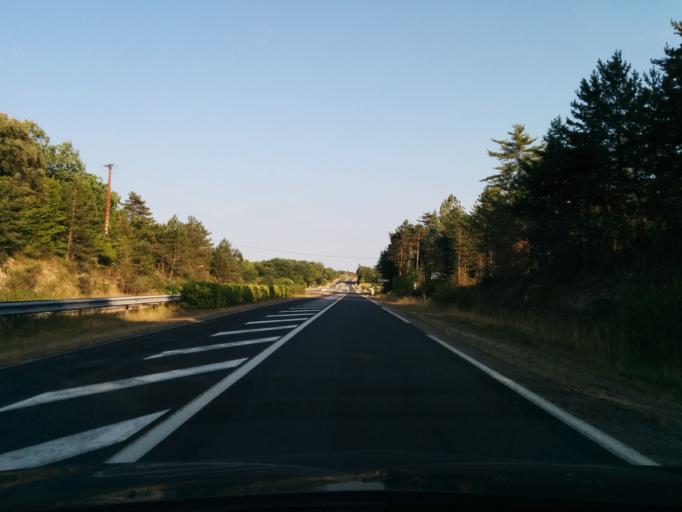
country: FR
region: Midi-Pyrenees
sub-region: Departement du Lot
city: Souillac
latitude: 44.8351
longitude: 1.4626
